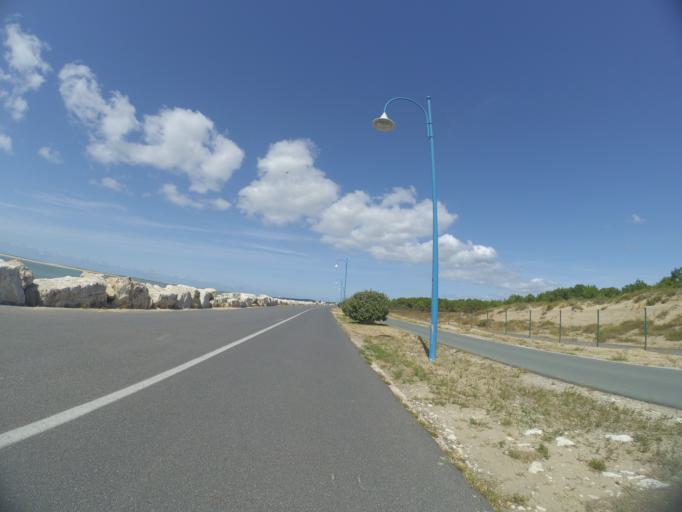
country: FR
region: Poitou-Charentes
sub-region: Departement de la Charente-Maritime
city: Les Mathes
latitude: 45.6784
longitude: -1.1729
